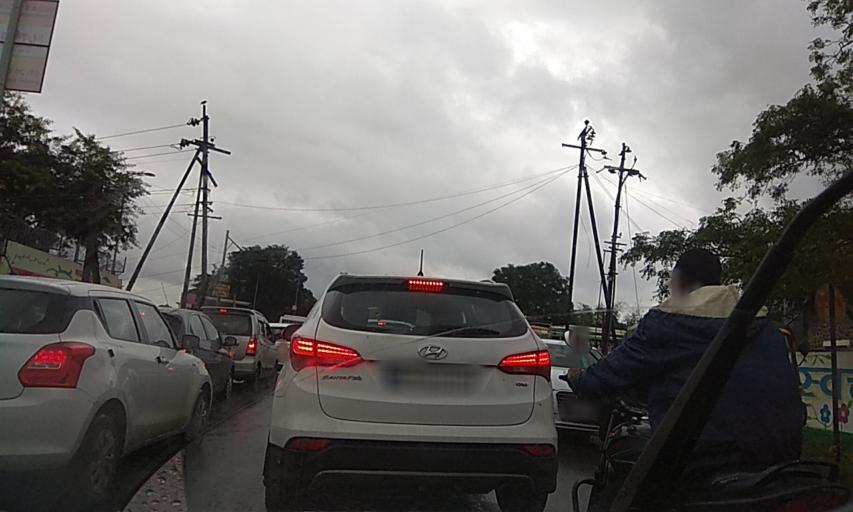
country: IN
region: Maharashtra
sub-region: Pune Division
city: Khadki
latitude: 18.5489
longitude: 73.8507
